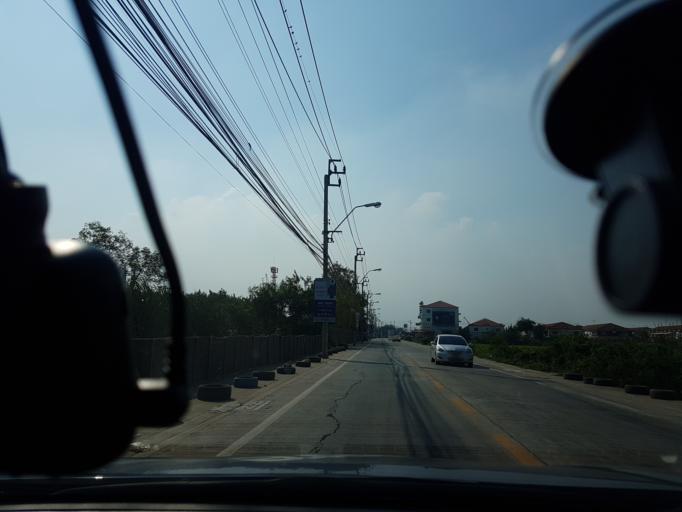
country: TH
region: Pathum Thani
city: Lam Luk Ka
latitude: 13.8968
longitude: 100.7216
